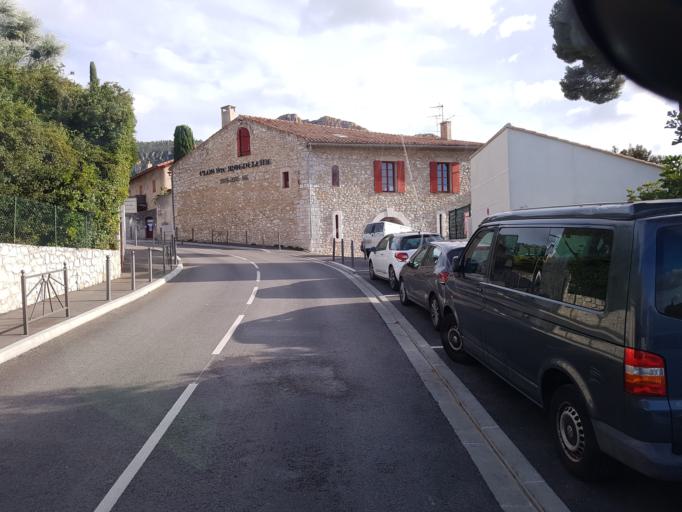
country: FR
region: Provence-Alpes-Cote d'Azur
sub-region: Departement des Bouches-du-Rhone
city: Cassis
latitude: 43.2115
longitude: 5.5450
